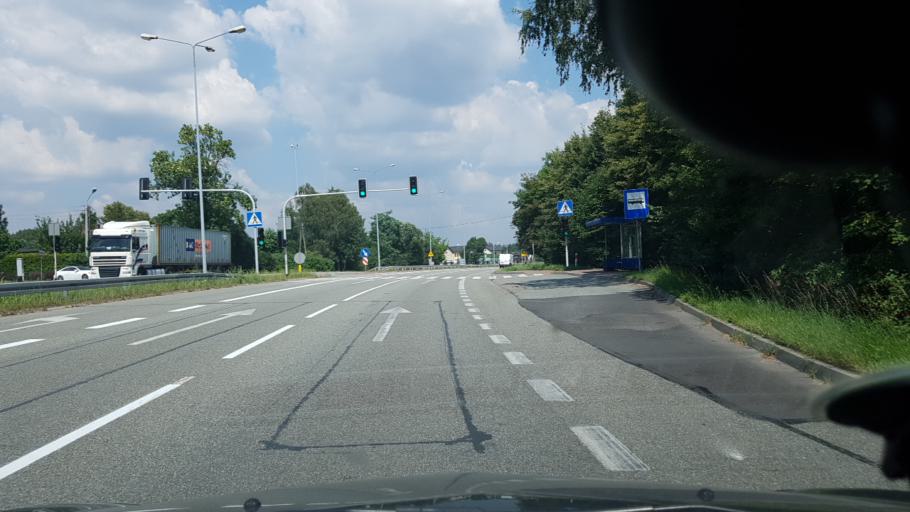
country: PL
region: Silesian Voivodeship
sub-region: Powiat mikolowski
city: Laziska Gorne
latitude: 50.1621
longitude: 18.8487
